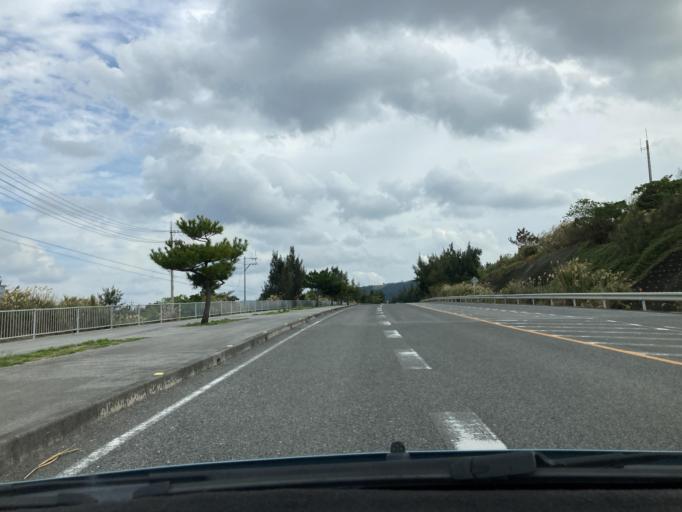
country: JP
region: Okinawa
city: Ishikawa
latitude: 26.4471
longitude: 127.8105
